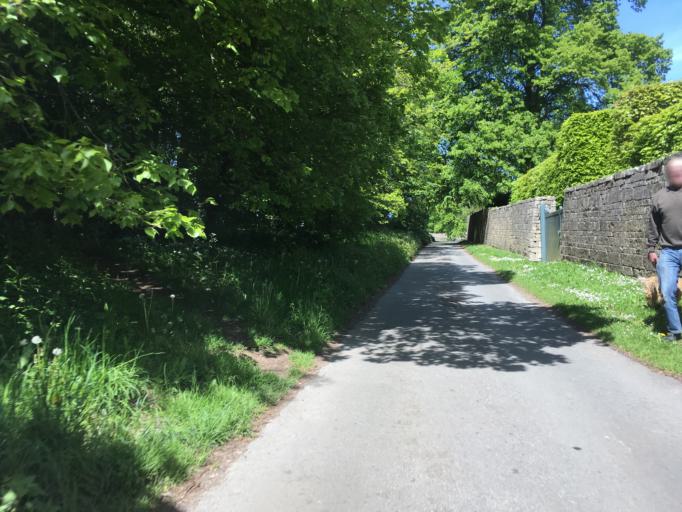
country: GB
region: England
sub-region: Gloucestershire
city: Brimscombe
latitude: 51.7314
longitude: -2.1851
